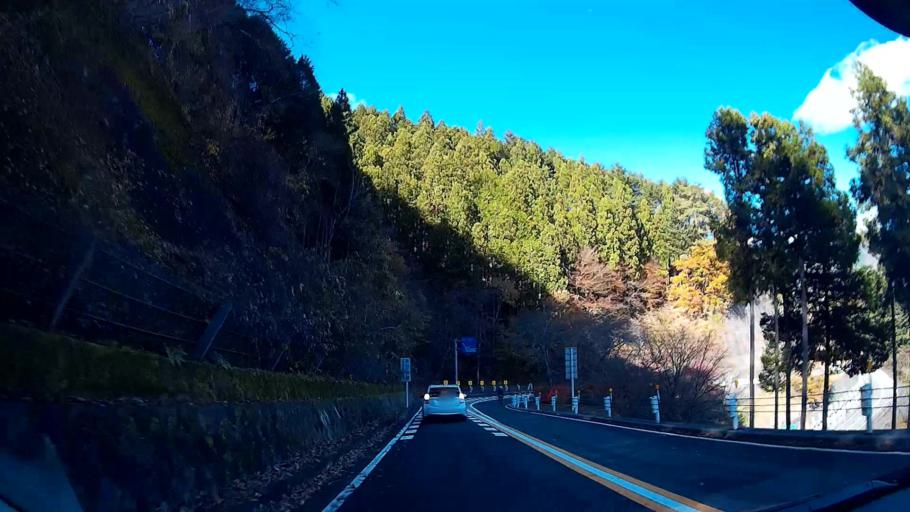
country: JP
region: Yamanashi
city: Uenohara
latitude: 35.7664
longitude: 139.0205
